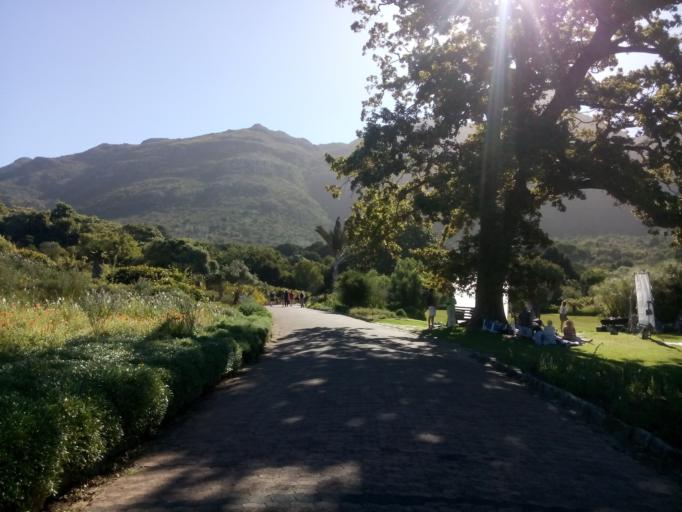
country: ZA
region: Western Cape
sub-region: City of Cape Town
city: Newlands
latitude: -33.9892
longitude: 18.4324
